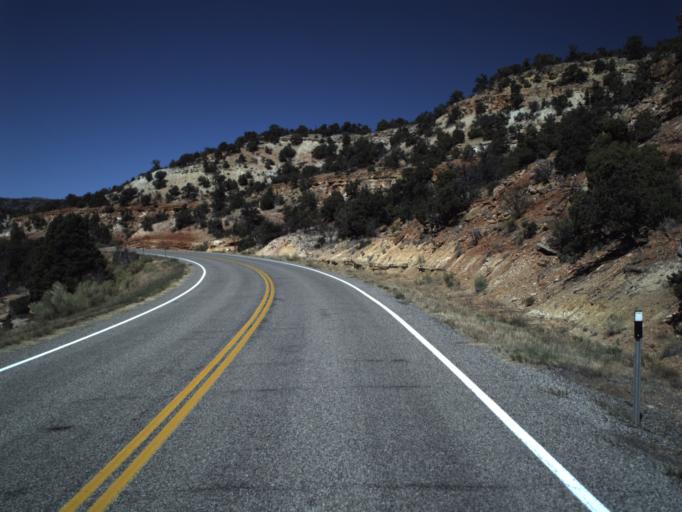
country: US
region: Utah
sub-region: Wayne County
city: Loa
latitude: 37.8909
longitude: -111.4513
